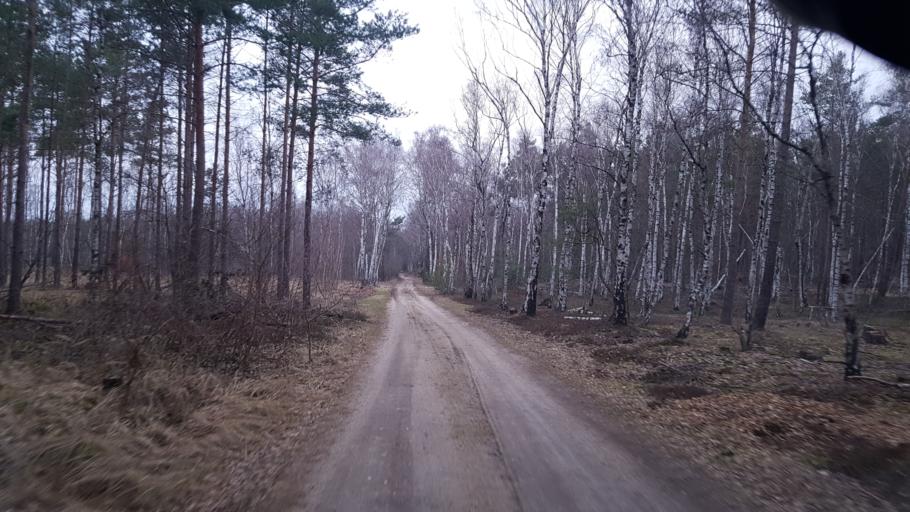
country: DE
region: Brandenburg
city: Trobitz
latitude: 51.6188
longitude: 13.4206
